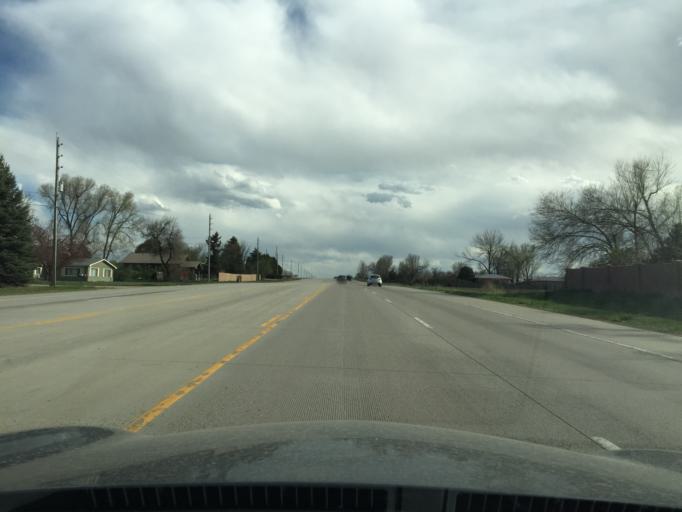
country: US
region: Colorado
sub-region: Boulder County
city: Longmont
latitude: 40.1299
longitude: -105.1027
